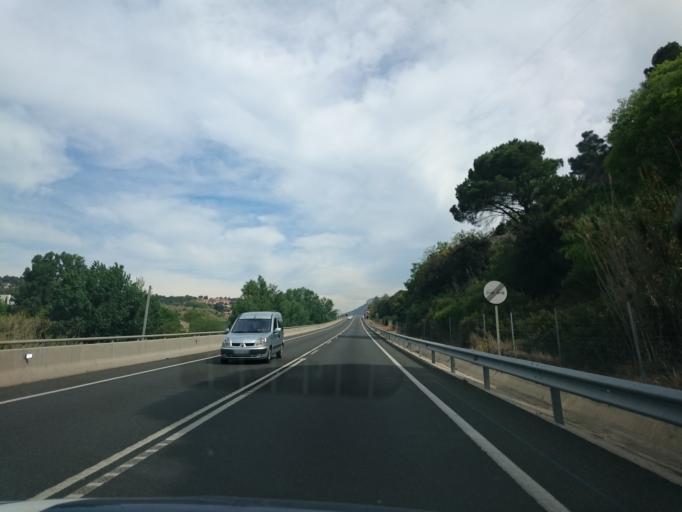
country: ES
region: Catalonia
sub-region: Provincia de Barcelona
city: Capellades
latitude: 41.5326
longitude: 1.6919
